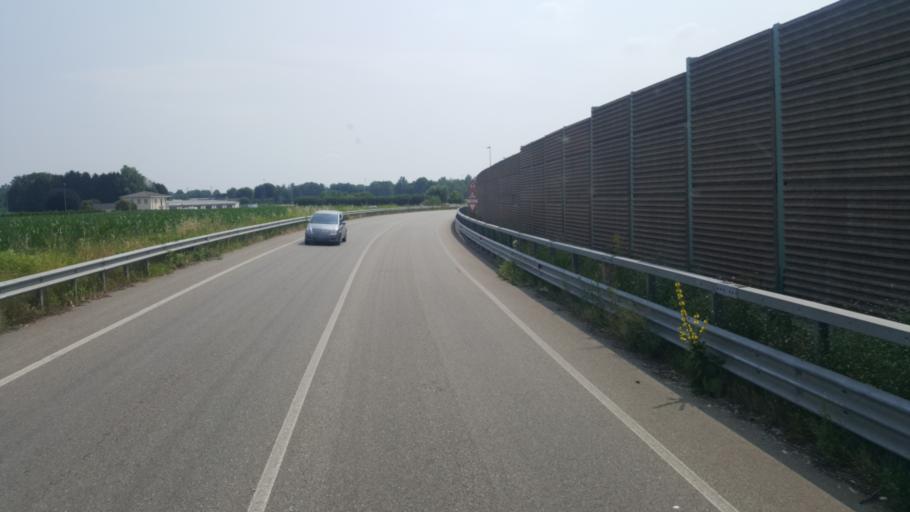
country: IT
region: Lombardy
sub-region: Provincia di Como
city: Luisago
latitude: 45.7669
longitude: 9.0310
